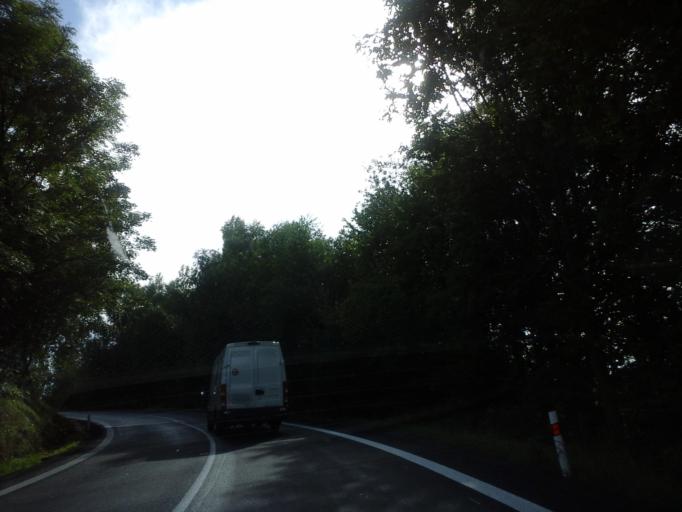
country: CZ
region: Olomoucky
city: Stity
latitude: 49.9552
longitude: 16.7004
